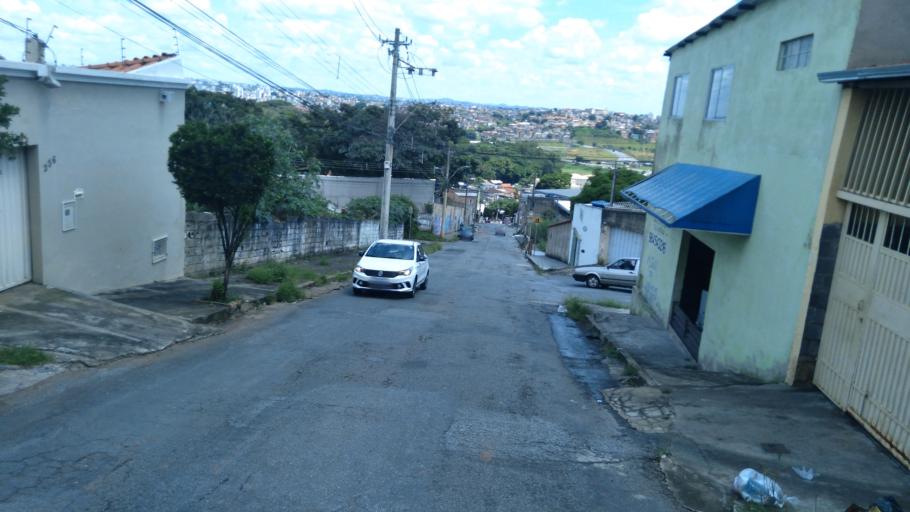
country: BR
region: Minas Gerais
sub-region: Belo Horizonte
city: Belo Horizonte
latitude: -19.8672
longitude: -43.9172
